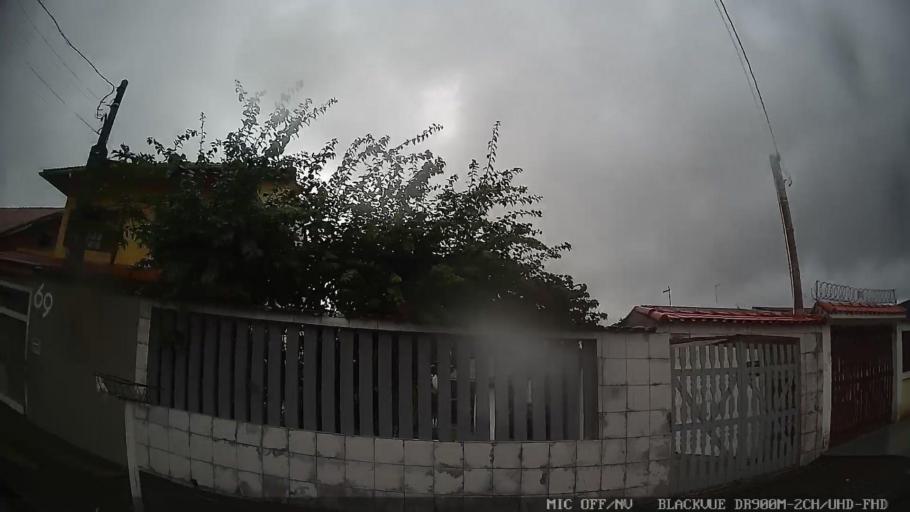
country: BR
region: Sao Paulo
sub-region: Itanhaem
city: Itanhaem
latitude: -24.1725
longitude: -46.7714
